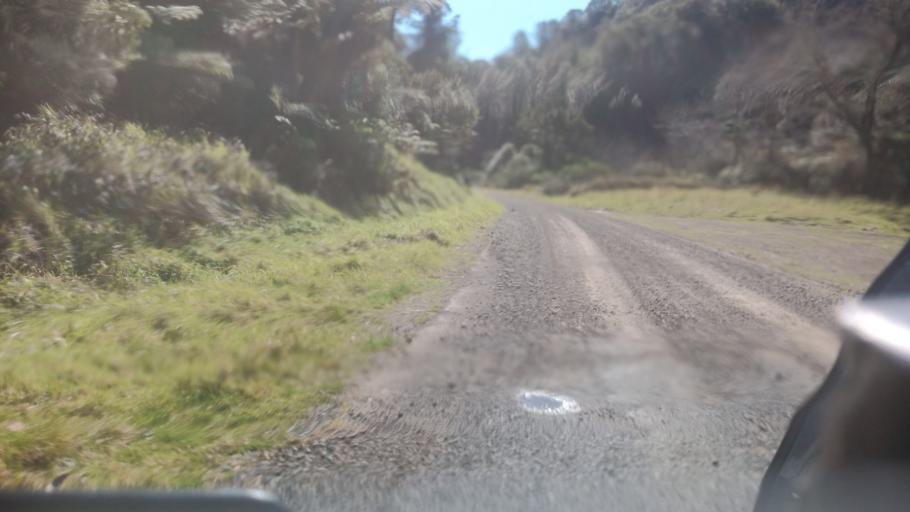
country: NZ
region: Bay of Plenty
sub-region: Opotiki District
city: Opotiki
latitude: -38.0473
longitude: 177.4500
